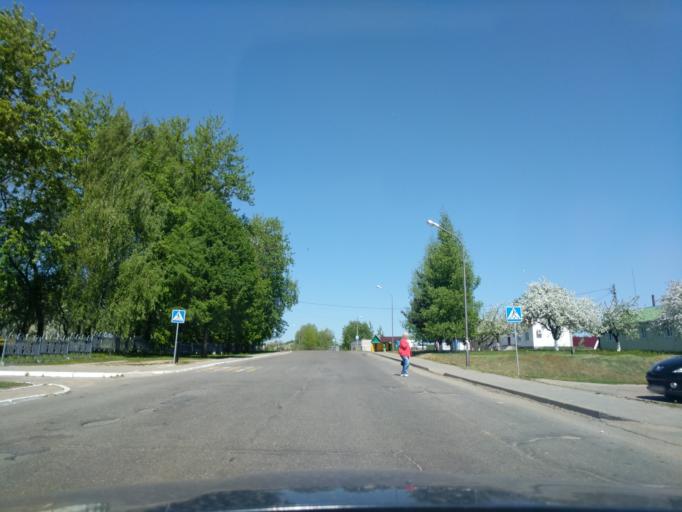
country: BY
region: Minsk
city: Myadzyel
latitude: 54.8873
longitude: 26.9156
